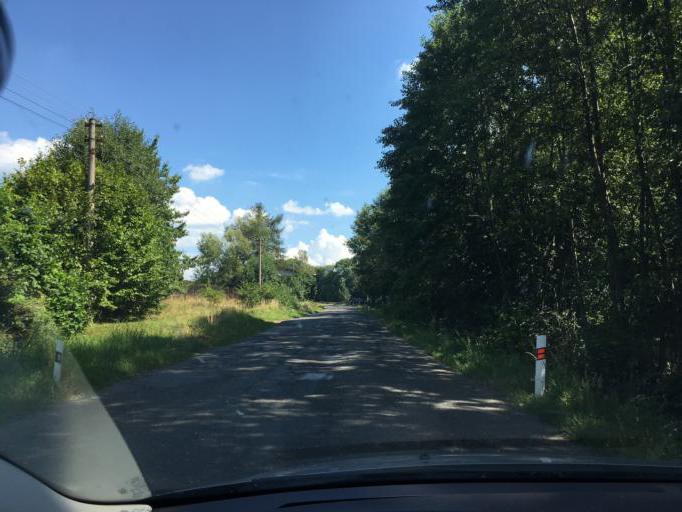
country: CZ
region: Liberecky
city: Hodkovice nad Mohelkou
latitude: 50.6572
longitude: 15.1337
